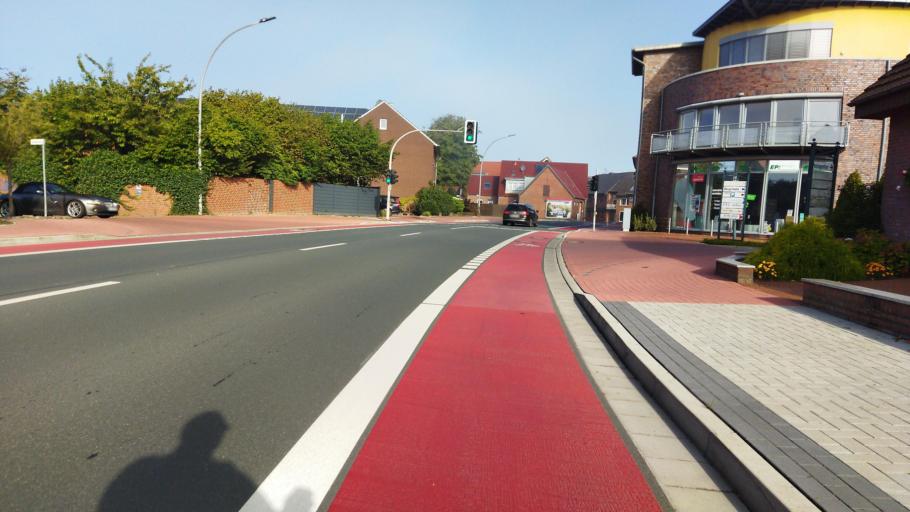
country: DE
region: North Rhine-Westphalia
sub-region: Regierungsbezirk Munster
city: Wettringen
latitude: 52.2074
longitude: 7.3186
